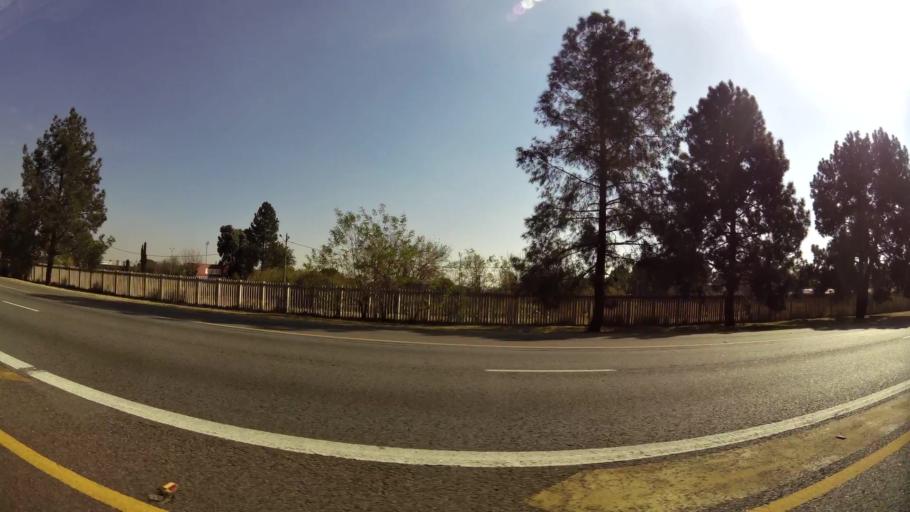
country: ZA
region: Gauteng
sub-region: City of Johannesburg Metropolitan Municipality
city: Modderfontein
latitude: -26.1279
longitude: 28.2304
